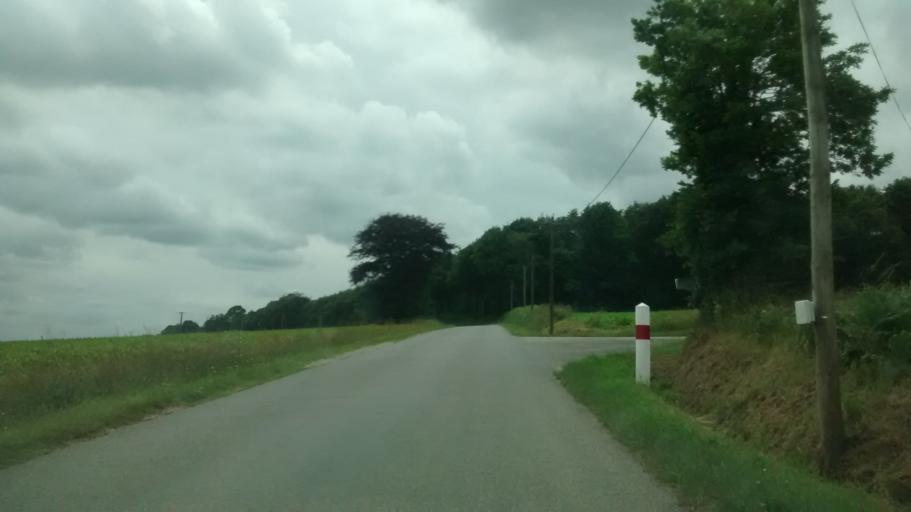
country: FR
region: Brittany
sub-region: Departement du Morbihan
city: Ruffiac
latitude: 47.8280
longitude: -2.2596
